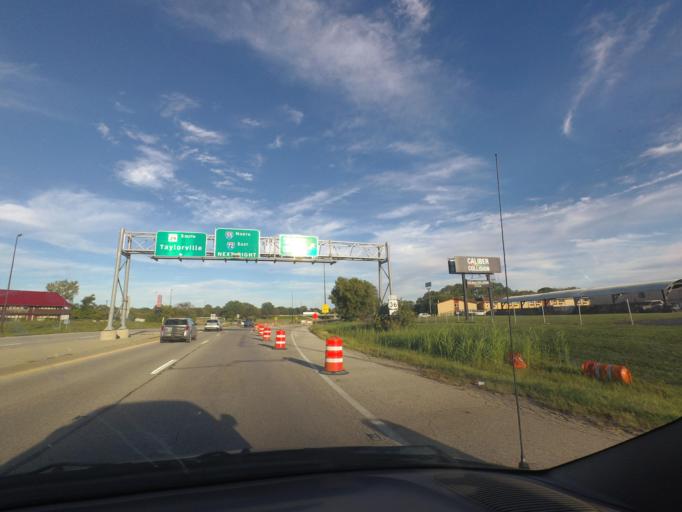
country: US
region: Illinois
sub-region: Sangamon County
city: Grandview
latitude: 39.7874
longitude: -89.6041
